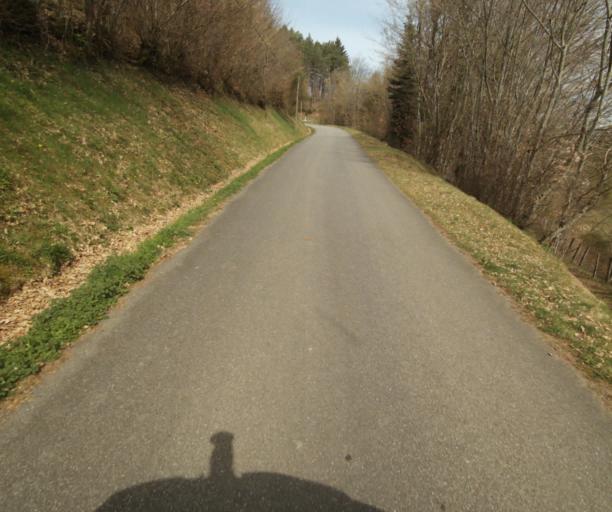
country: FR
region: Limousin
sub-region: Departement de la Correze
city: Naves
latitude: 45.3246
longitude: 1.8063
